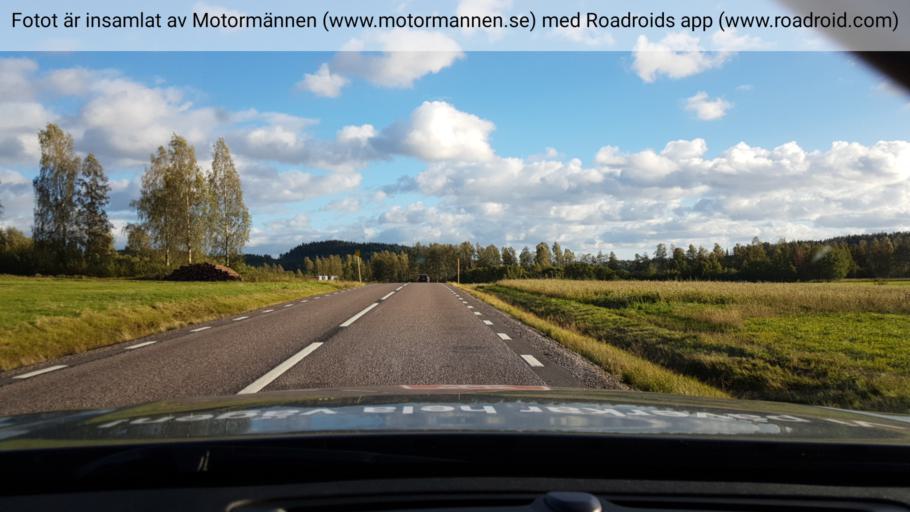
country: SE
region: Vaermland
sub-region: Karlstads Kommun
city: Molkom
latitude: 59.6715
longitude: 13.6886
